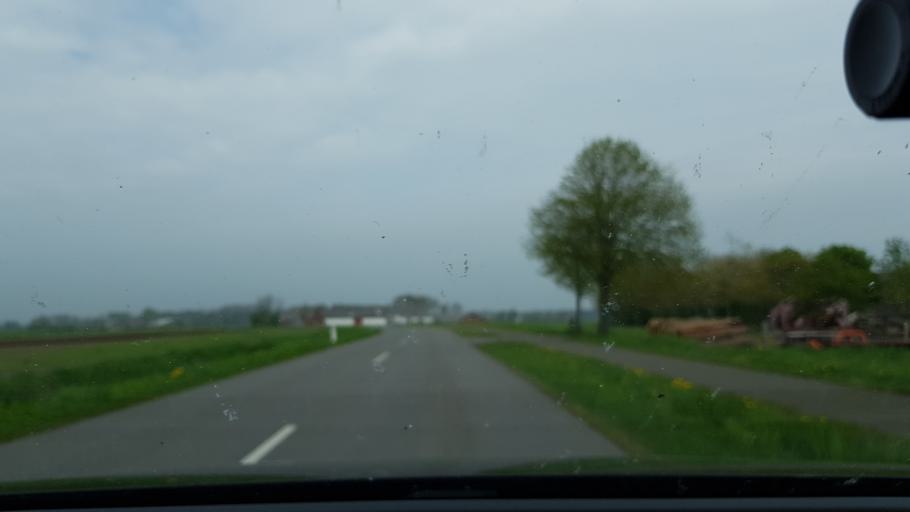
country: DK
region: Capital Region
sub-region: Bornholm Kommune
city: Nexo
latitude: 55.0094
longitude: 15.0943
